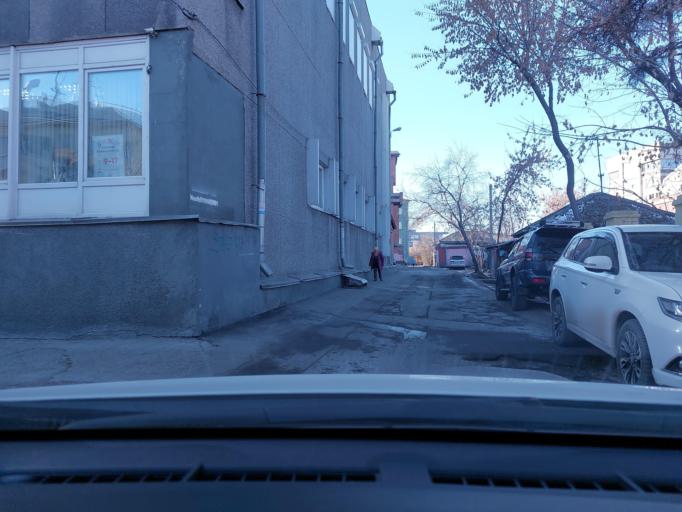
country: RU
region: Irkutsk
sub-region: Irkutskiy Rayon
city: Irkutsk
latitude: 52.2873
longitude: 104.2761
